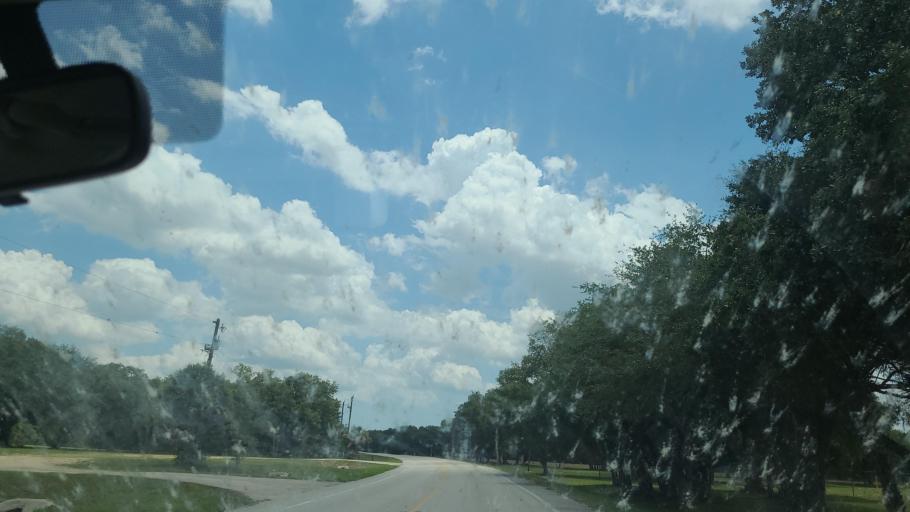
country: US
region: Florida
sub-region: Glades County
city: Buckhead Ridge
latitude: 27.1209
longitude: -81.0820
